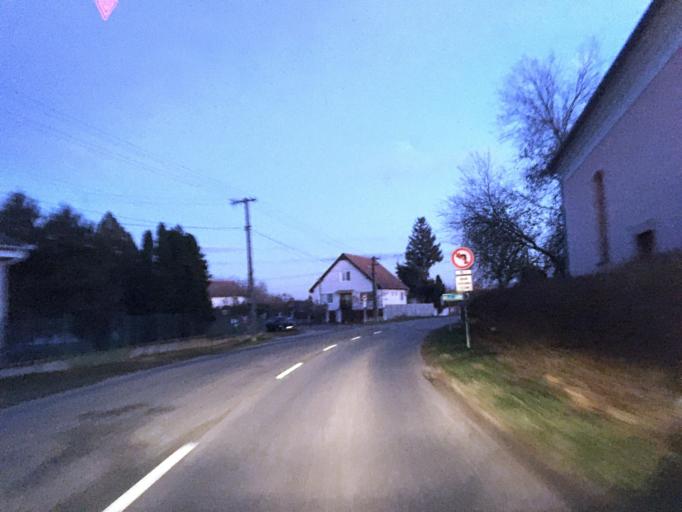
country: SK
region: Nitriansky
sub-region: Okres Komarno
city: Hurbanovo
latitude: 47.9003
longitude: 18.1412
